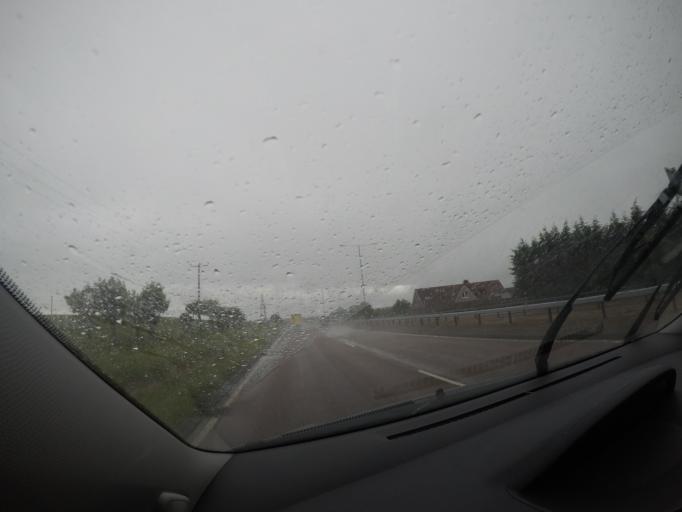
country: GB
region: Scotland
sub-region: Dundee City
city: Dundee
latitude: 56.5227
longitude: -2.9444
